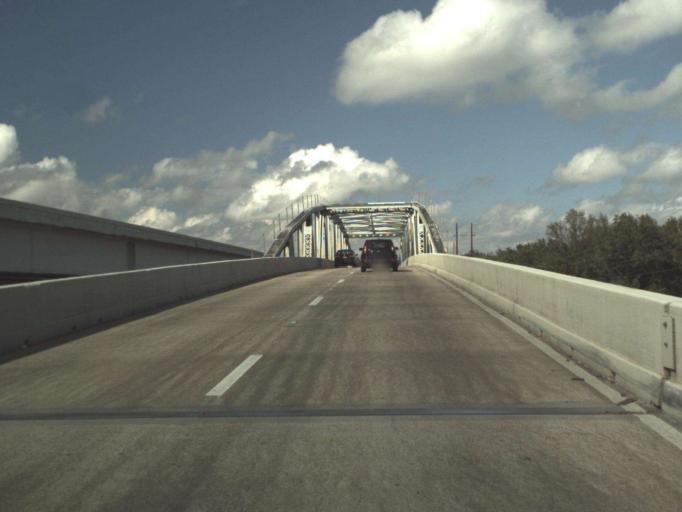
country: US
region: Florida
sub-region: Liberty County
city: Bristol
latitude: 30.4363
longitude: -85.0003
